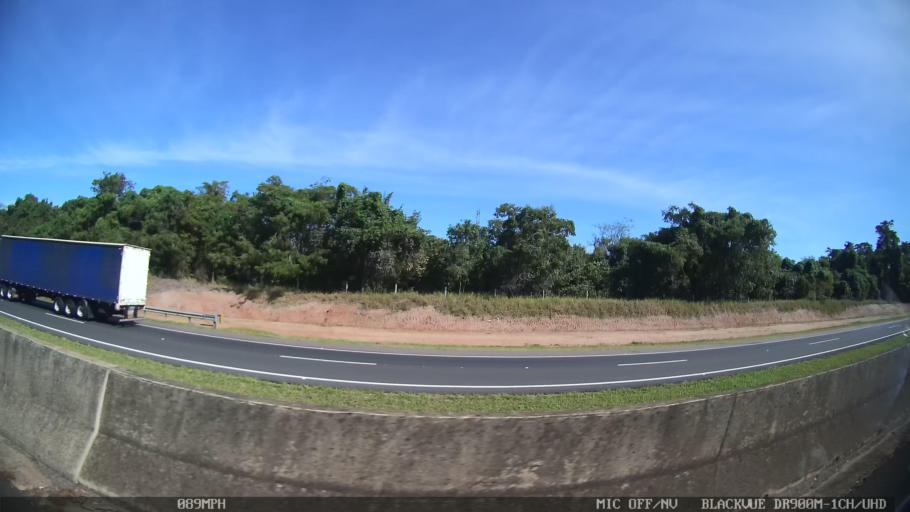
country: BR
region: Sao Paulo
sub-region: Pirassununga
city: Pirassununga
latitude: -21.9375
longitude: -47.4665
